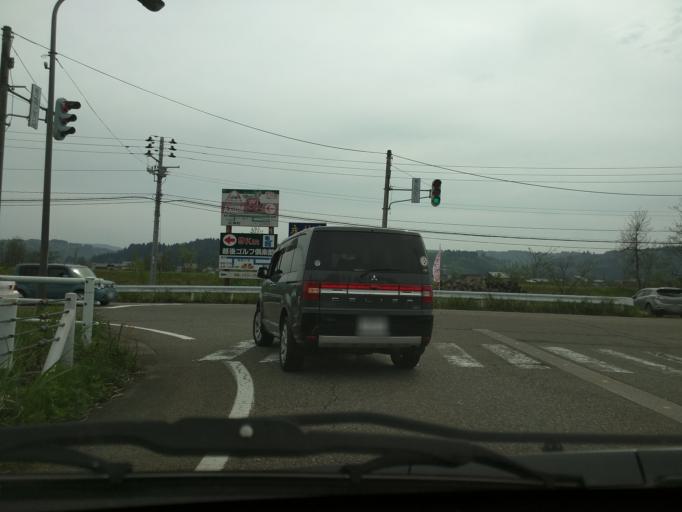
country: JP
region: Niigata
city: Ojiya
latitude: 37.2553
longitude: 138.9204
